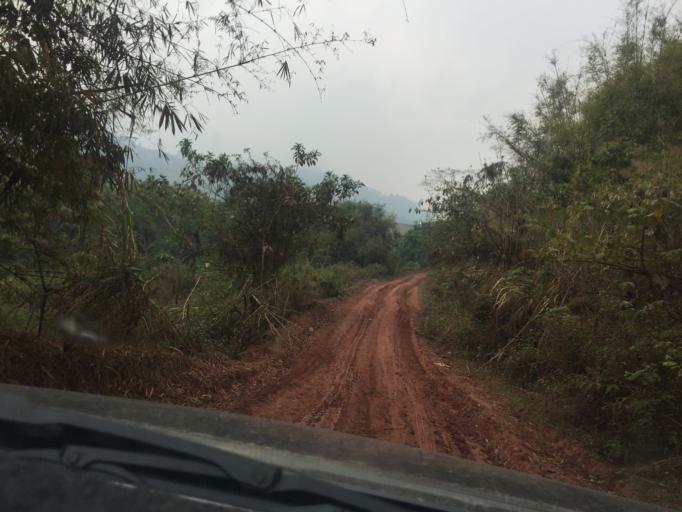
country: TH
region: Nan
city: Bo Kluea
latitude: 18.8463
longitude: 101.4112
